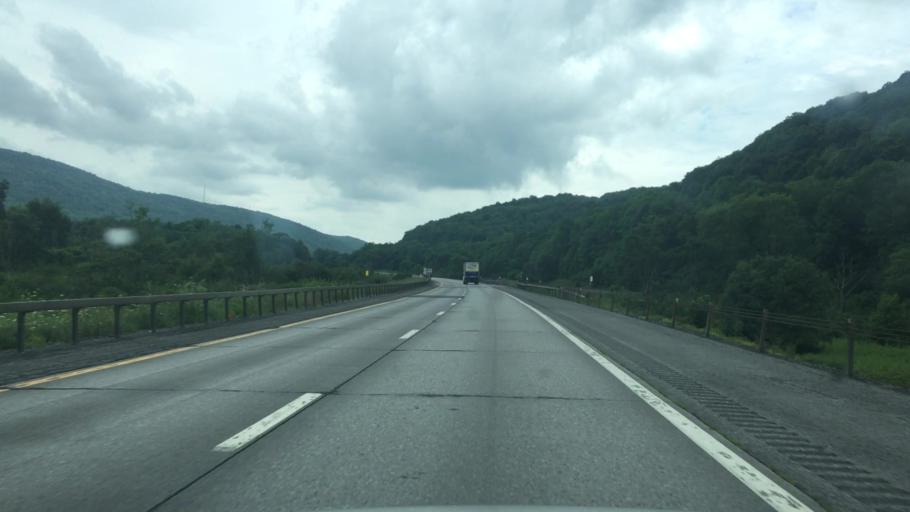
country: US
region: New York
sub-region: Otsego County
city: Worcester
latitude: 42.6051
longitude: -74.6964
